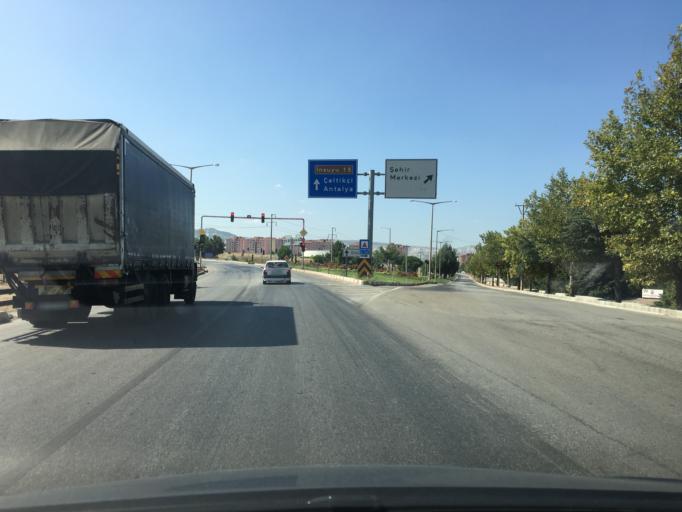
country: TR
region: Burdur
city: Burdur
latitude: 37.7417
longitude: 30.3130
